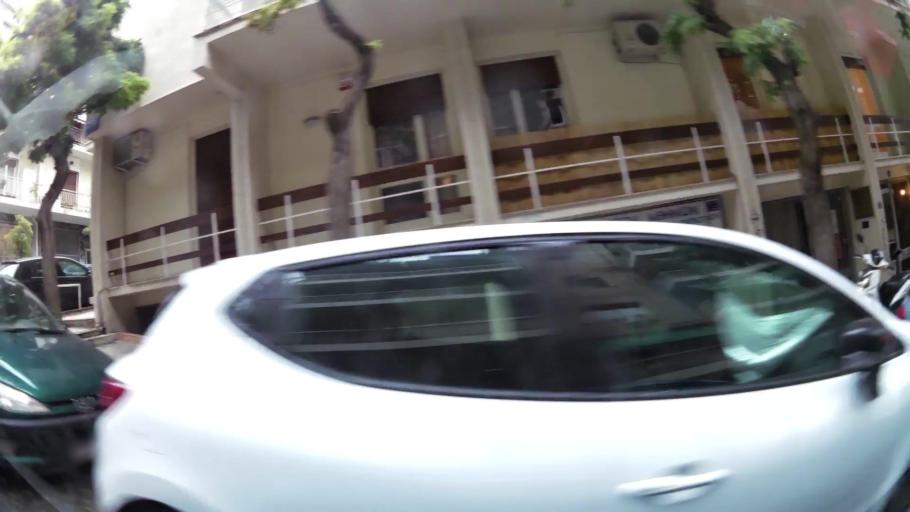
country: GR
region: Attica
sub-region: Nomarchia Athinas
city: Vyronas
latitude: 37.9709
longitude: 23.7439
